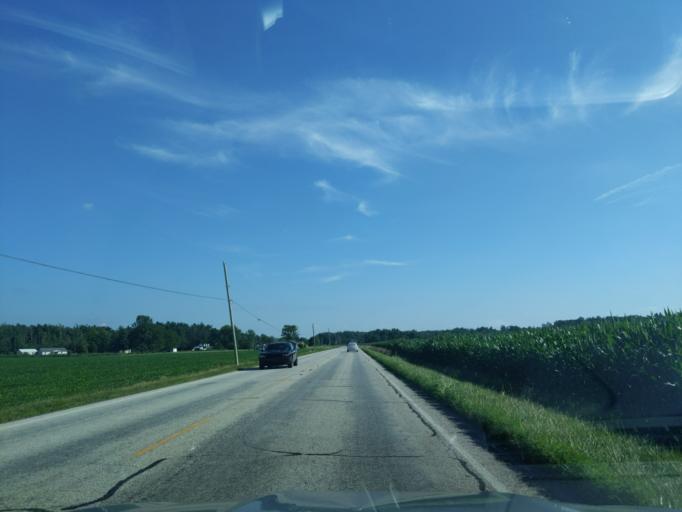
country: US
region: Indiana
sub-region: Ripley County
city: Osgood
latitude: 39.1100
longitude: -85.2798
